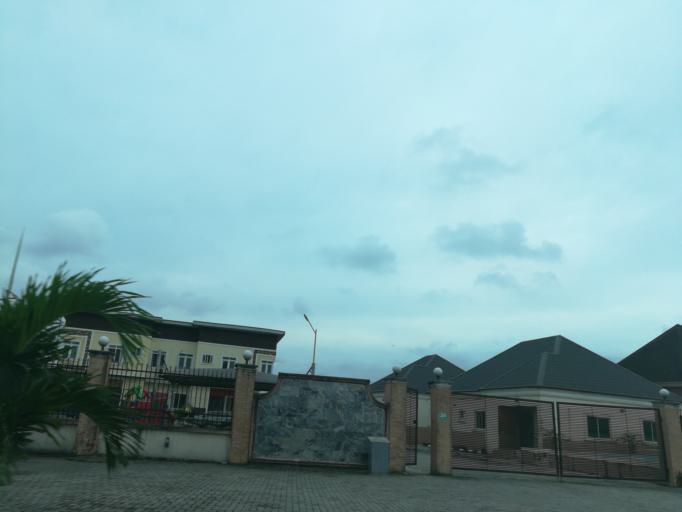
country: NG
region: Rivers
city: Port Harcourt
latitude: 4.8098
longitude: 6.9936
